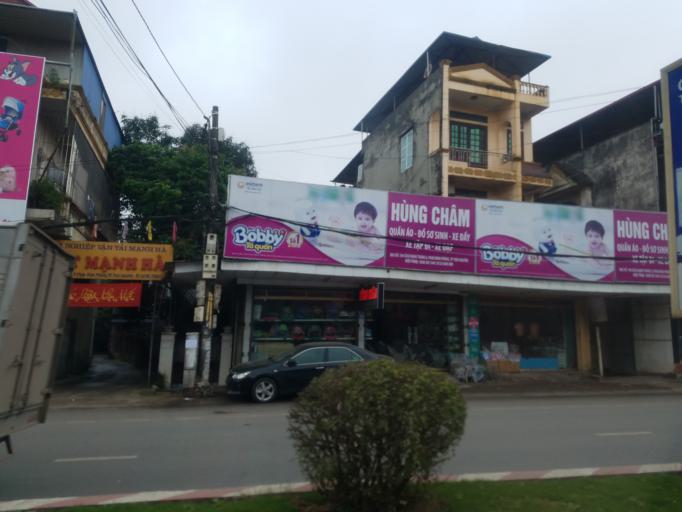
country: VN
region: Thai Nguyen
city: Thanh Pho Thai Nguyen
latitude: 21.5920
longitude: 105.8435
